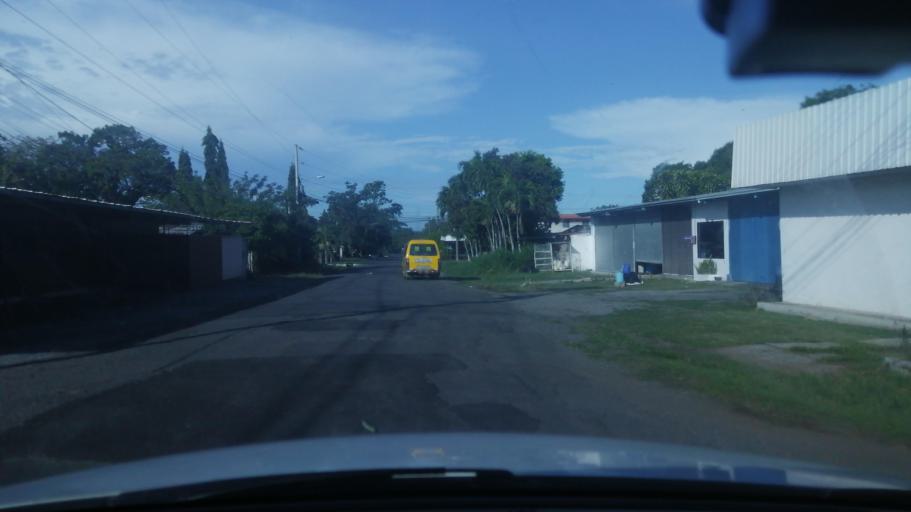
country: PA
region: Chiriqui
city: David
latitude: 8.4347
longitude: -82.4346
